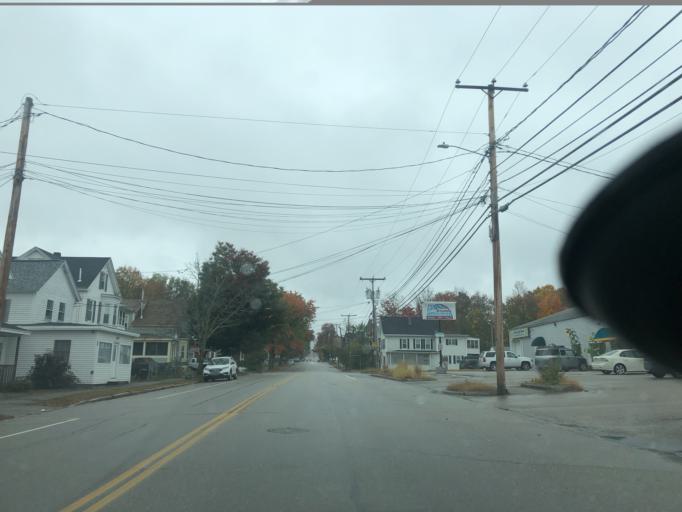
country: US
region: New Hampshire
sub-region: Strafford County
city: Dover
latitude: 43.2024
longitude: -70.8708
